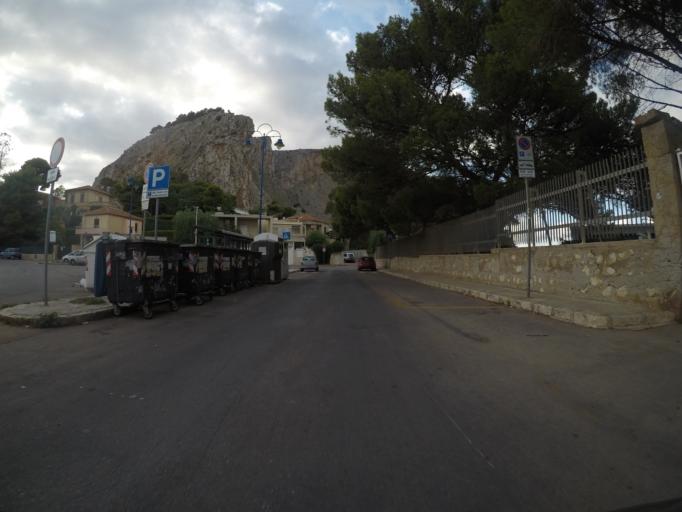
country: IT
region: Sicily
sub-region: Palermo
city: Palermo
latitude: 38.2106
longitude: 13.3282
